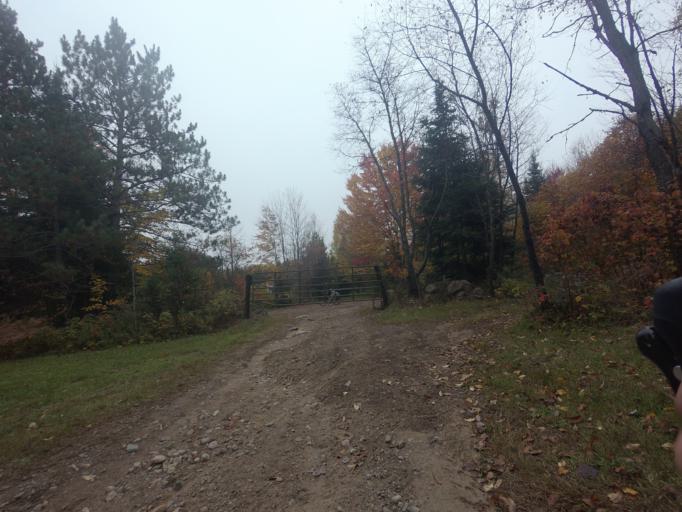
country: CA
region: Ontario
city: Petawawa
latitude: 45.7478
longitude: -77.3494
